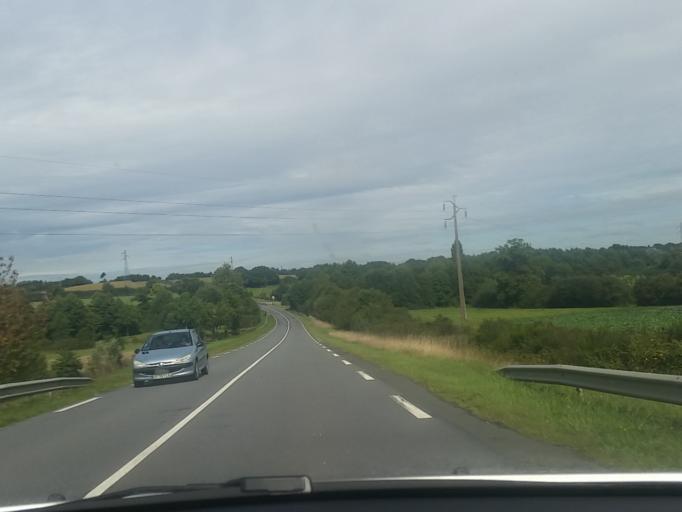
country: FR
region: Pays de la Loire
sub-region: Departement de la Loire-Atlantique
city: Chateaubriant
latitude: 47.7228
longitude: -1.3569
